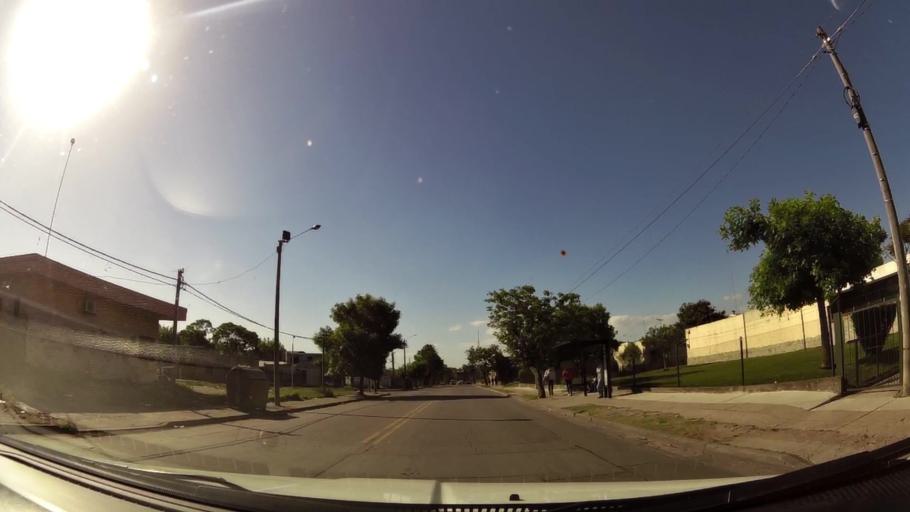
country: UY
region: Montevideo
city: Montevideo
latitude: -34.8366
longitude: -56.1497
